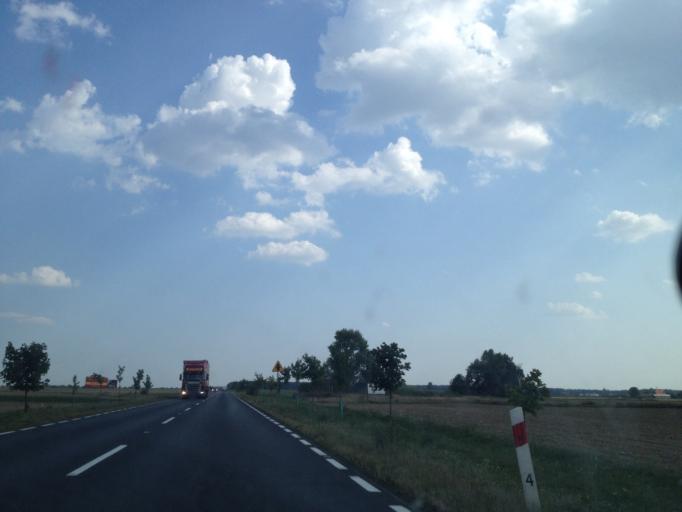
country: PL
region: Greater Poland Voivodeship
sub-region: Powiat poznanski
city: Kornik
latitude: 52.2367
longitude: 17.0598
